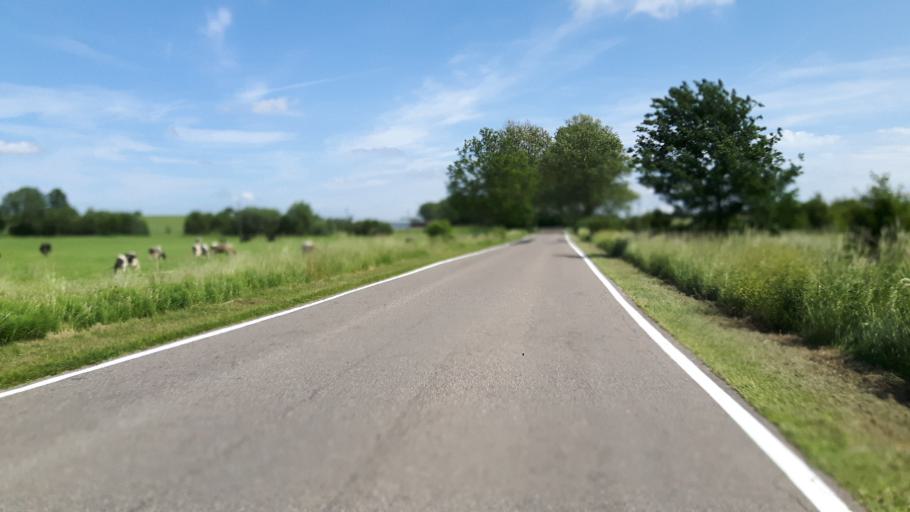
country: PL
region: Pomeranian Voivodeship
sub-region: Powiat wejherowski
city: Gniewino
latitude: 54.7215
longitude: 17.9821
